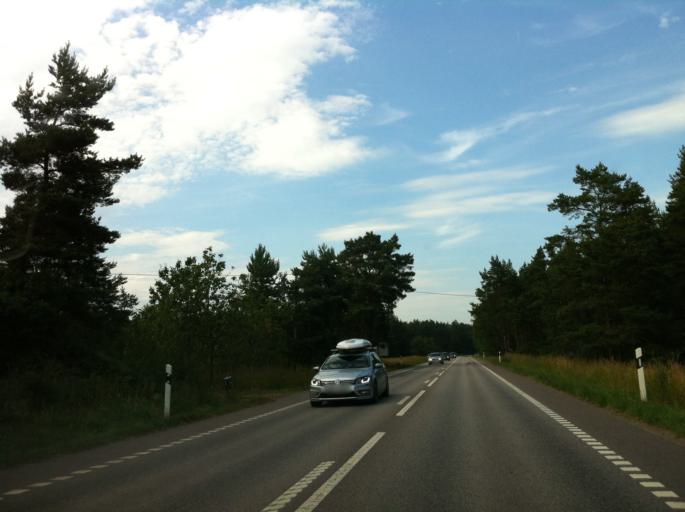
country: SE
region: Kalmar
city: Faerjestaden
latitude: 56.7461
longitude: 16.5478
